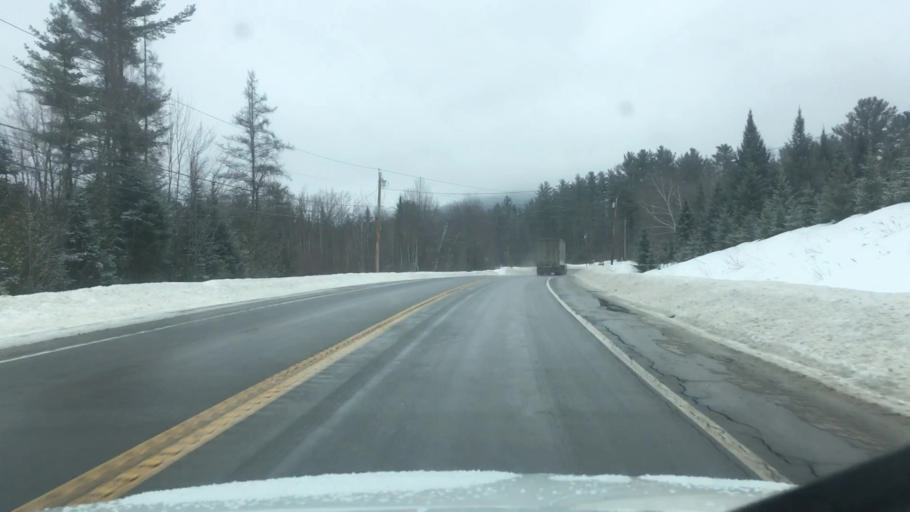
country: US
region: Maine
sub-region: Oxford County
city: Peru
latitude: 44.5589
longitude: -70.3777
